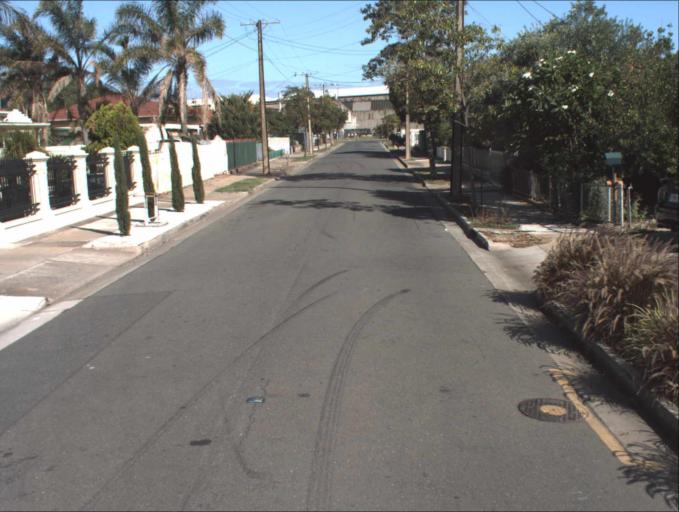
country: AU
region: South Australia
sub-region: Port Adelaide Enfield
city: Alberton
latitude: -34.8474
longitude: 138.5405
